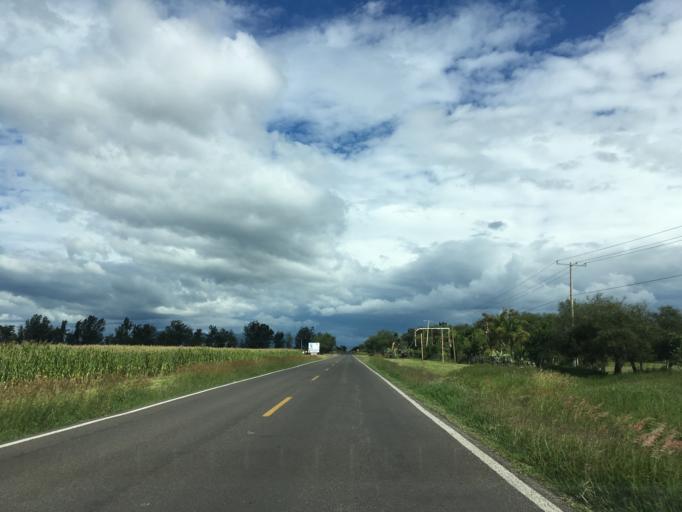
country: MX
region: Michoacan
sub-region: Cuitzeo
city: Cuamio
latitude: 20.0611
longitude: -101.1020
